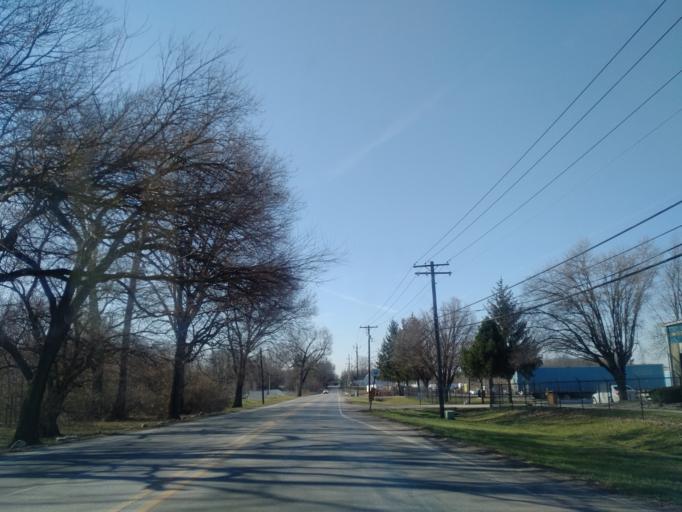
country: US
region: Indiana
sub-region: Marion County
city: Indianapolis
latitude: 39.7217
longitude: -86.1683
